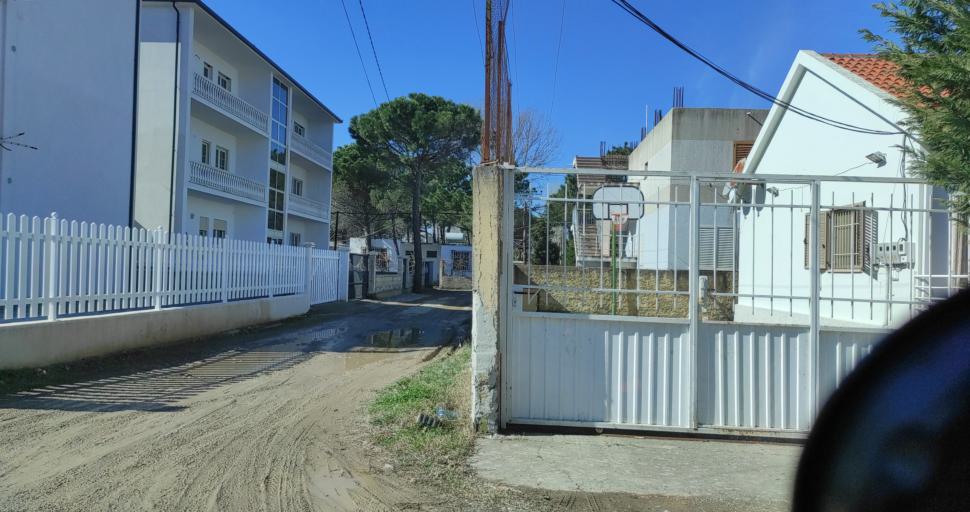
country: AL
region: Shkoder
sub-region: Rrethi i Shkodres
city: Velipoje
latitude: 41.8642
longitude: 19.4102
